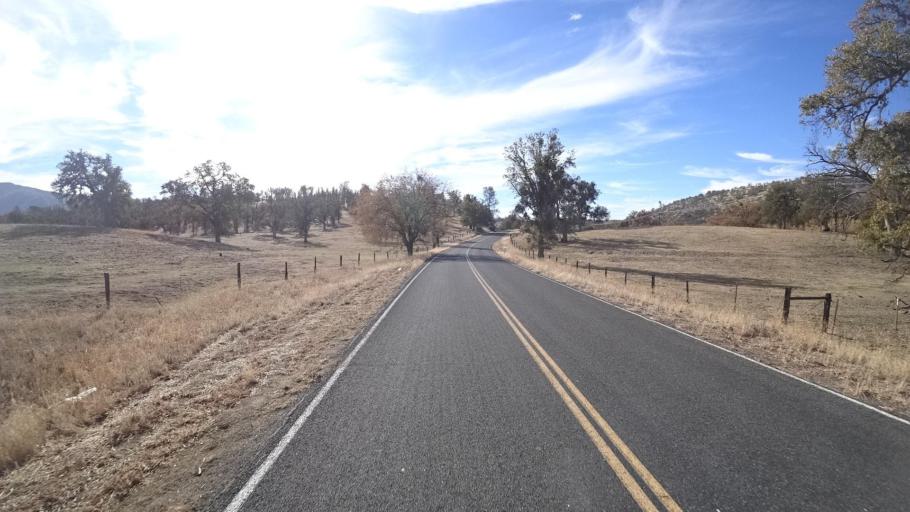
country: US
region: California
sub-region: Kern County
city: Alta Sierra
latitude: 35.6807
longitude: -118.7343
